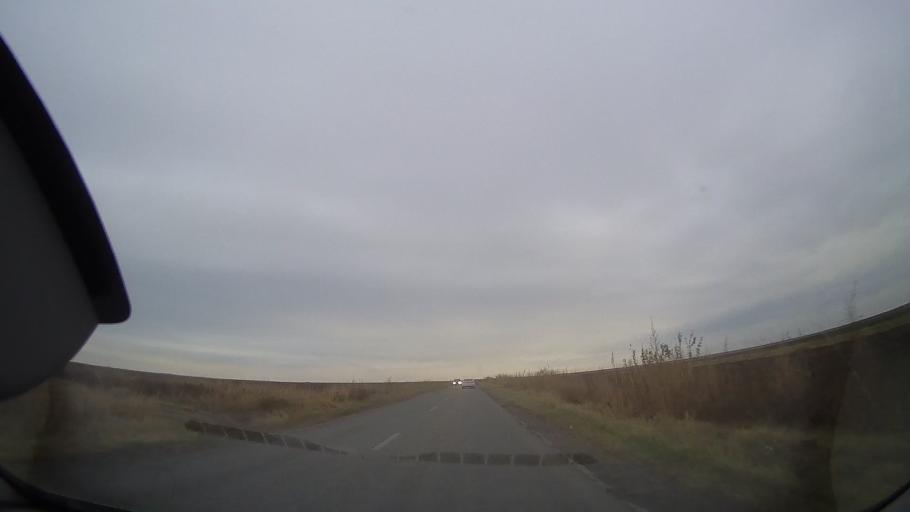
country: RO
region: Ialomita
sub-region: Oras Amara
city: Amara
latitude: 44.6632
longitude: 27.3007
